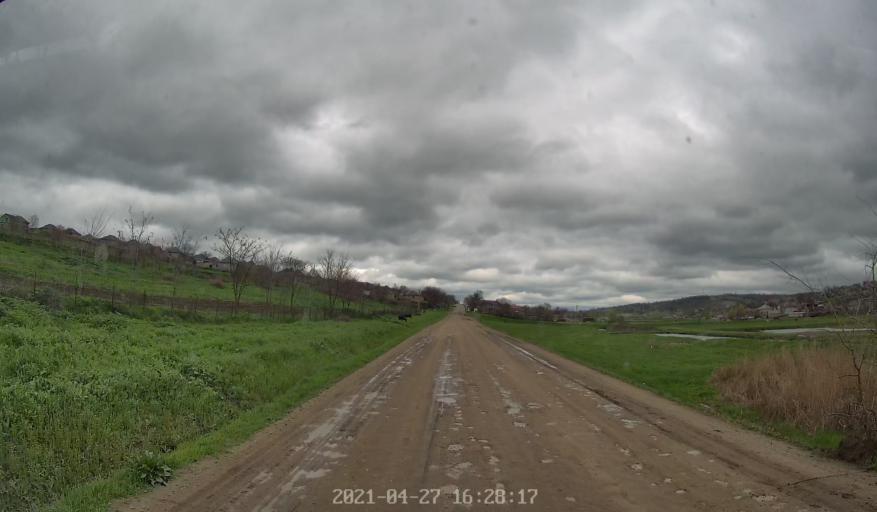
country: MD
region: Chisinau
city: Singera
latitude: 46.9723
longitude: 29.0409
